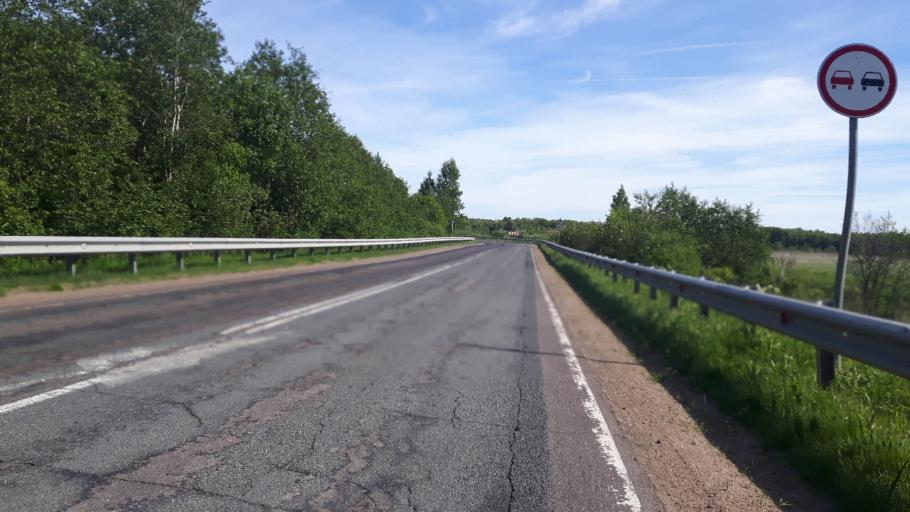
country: RU
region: Leningrad
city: Ivangorod
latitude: 59.4165
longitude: 28.3258
